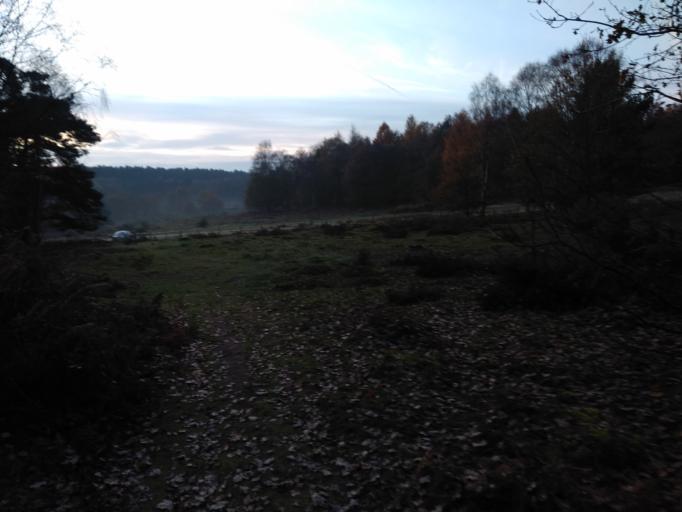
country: GB
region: England
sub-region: Nottinghamshire
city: Worksop
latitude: 53.2686
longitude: -1.0730
